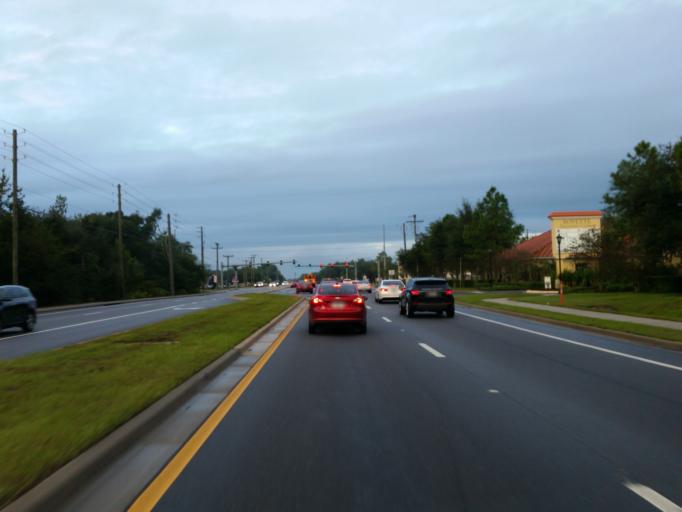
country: US
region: Florida
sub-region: Hillsborough County
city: Riverview
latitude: 27.8536
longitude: -82.2999
